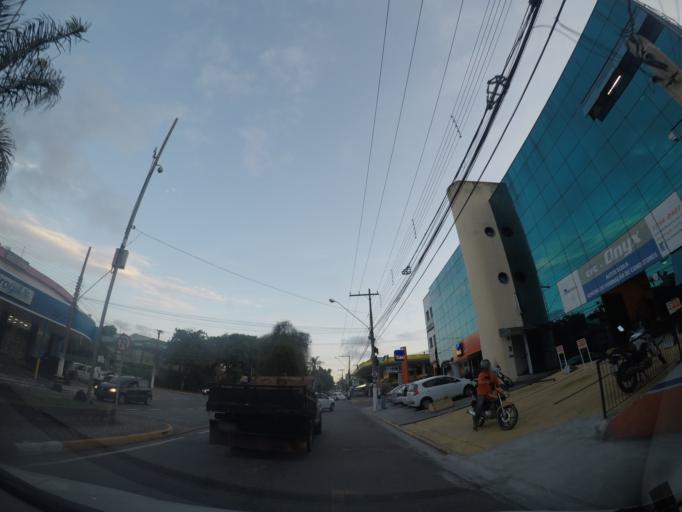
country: BR
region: Sao Paulo
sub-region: Aruja
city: Aruja
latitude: -23.3975
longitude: -46.3200
